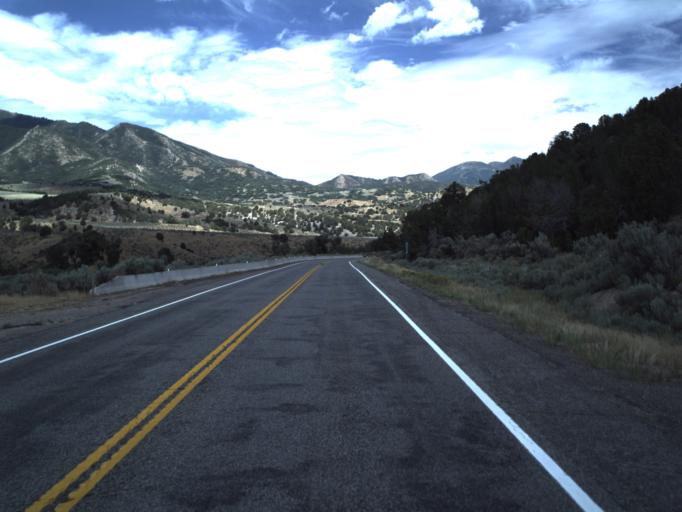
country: US
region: Utah
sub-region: Utah County
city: Woodland Hills
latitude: 39.9323
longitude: -111.5437
